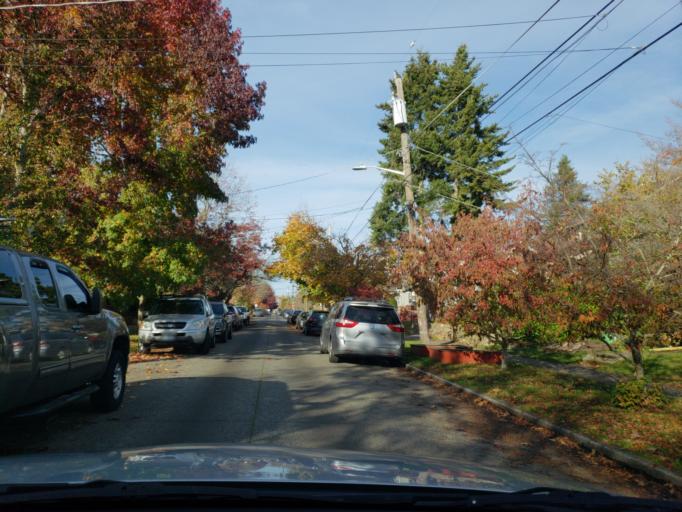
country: US
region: Washington
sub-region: King County
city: Shoreline
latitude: 47.6856
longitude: -122.3741
